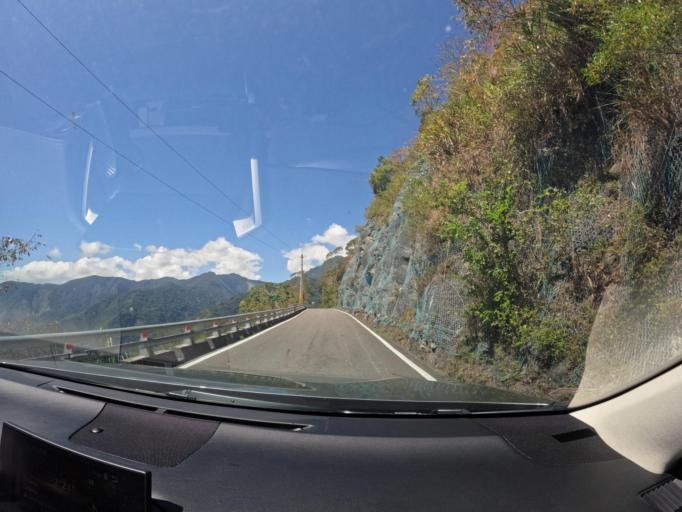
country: TW
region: Taiwan
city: Yujing
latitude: 23.2786
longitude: 120.8384
